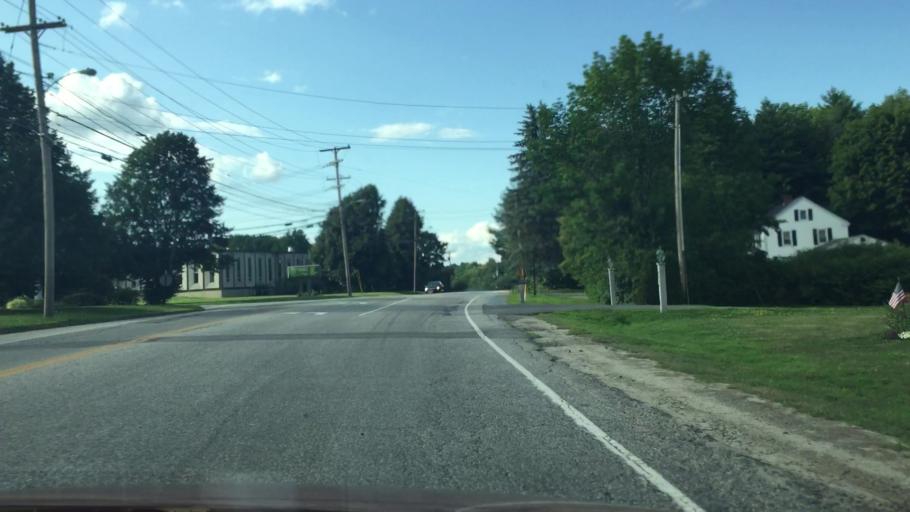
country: US
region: Maine
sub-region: Cumberland County
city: Westbrook
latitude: 43.6580
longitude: -70.3616
